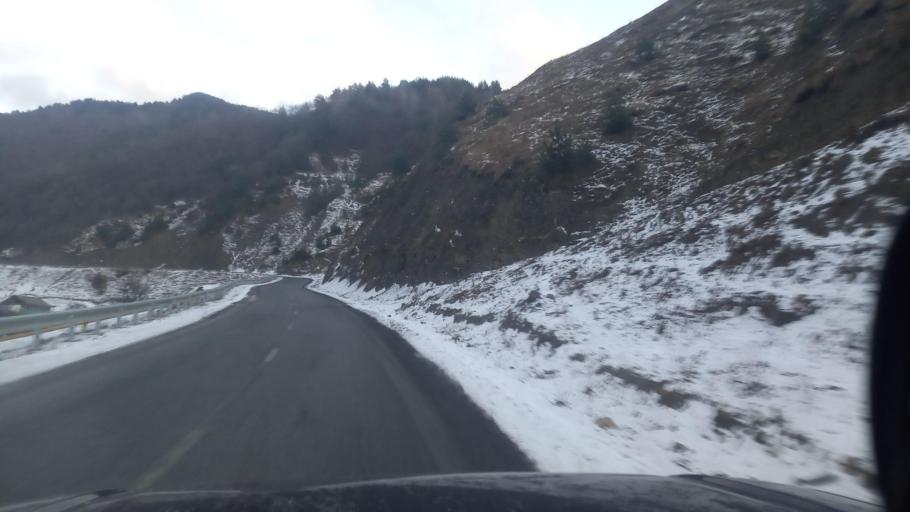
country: RU
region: Ingushetiya
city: Dzhayrakh
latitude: 42.8113
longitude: 44.8017
